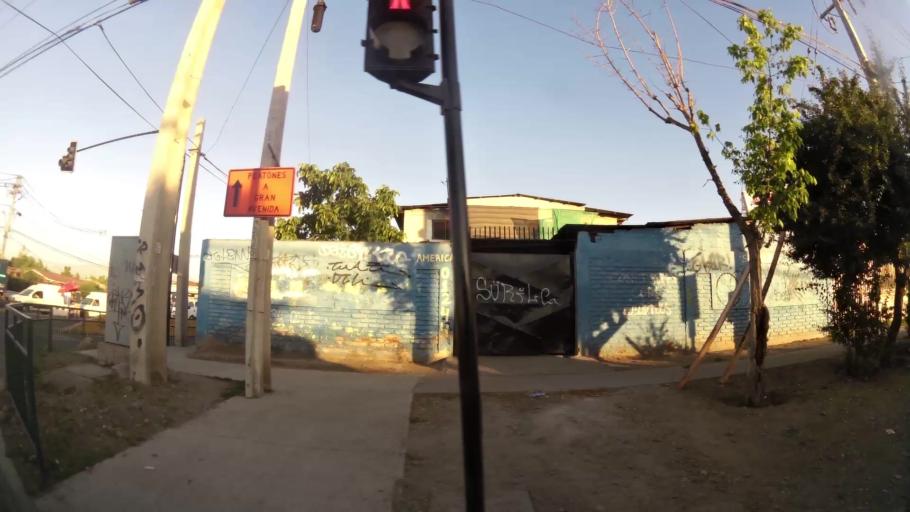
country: CL
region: Santiago Metropolitan
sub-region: Provincia de Maipo
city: San Bernardo
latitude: -33.5731
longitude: -70.7008
